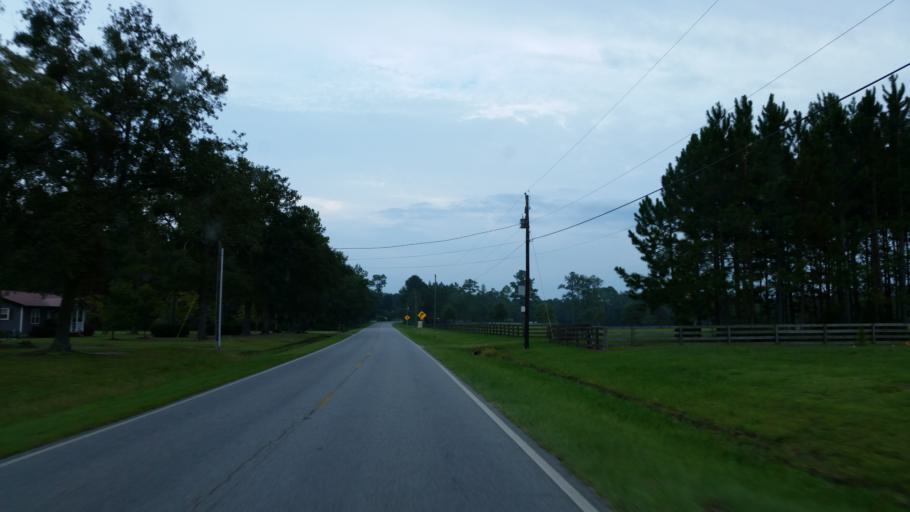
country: US
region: Georgia
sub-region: Lowndes County
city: Valdosta
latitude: 30.7611
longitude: -83.2625
